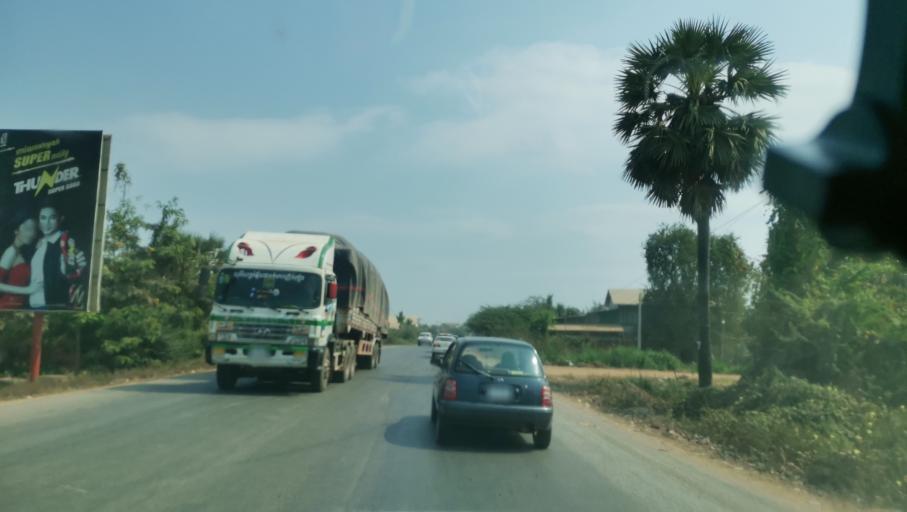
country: KH
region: Battambang
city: Battambang
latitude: 13.0726
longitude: 103.1703
